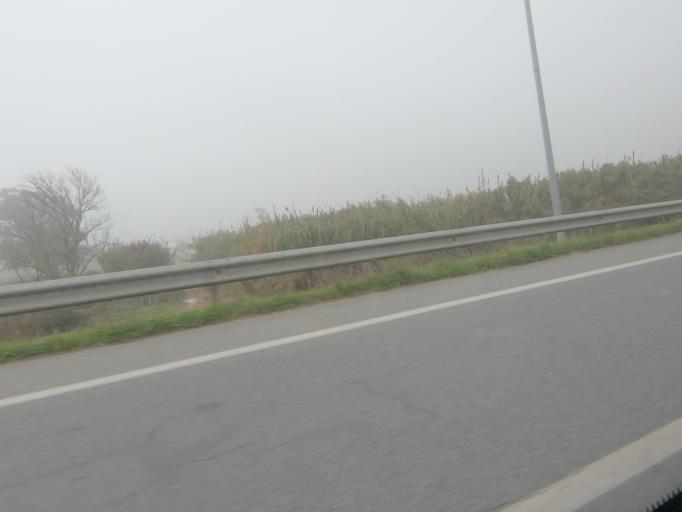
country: PT
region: Setubal
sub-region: Montijo
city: Montijo
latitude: 38.6805
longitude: -8.9471
